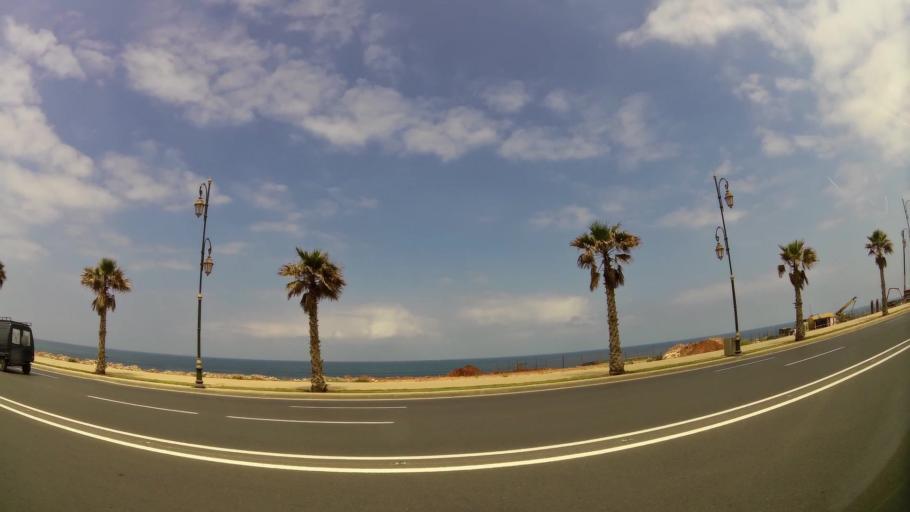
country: MA
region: Rabat-Sale-Zemmour-Zaer
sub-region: Skhirate-Temara
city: Temara
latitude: 33.9868
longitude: -6.8891
